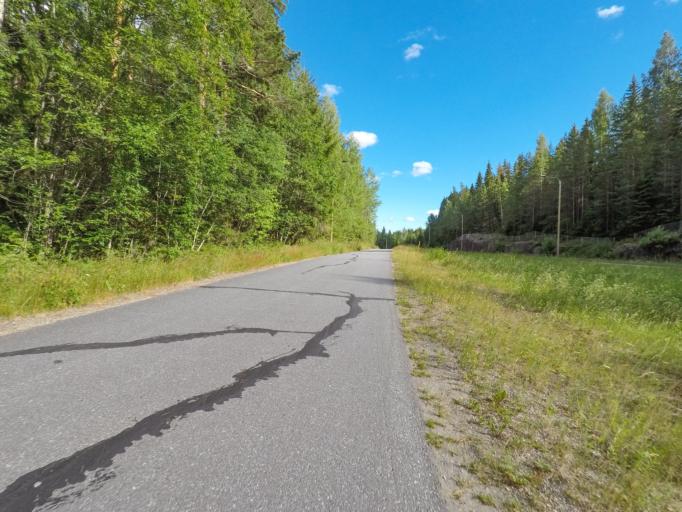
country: FI
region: South Karelia
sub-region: Lappeenranta
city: Lappeenranta
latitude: 61.1040
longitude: 28.1231
